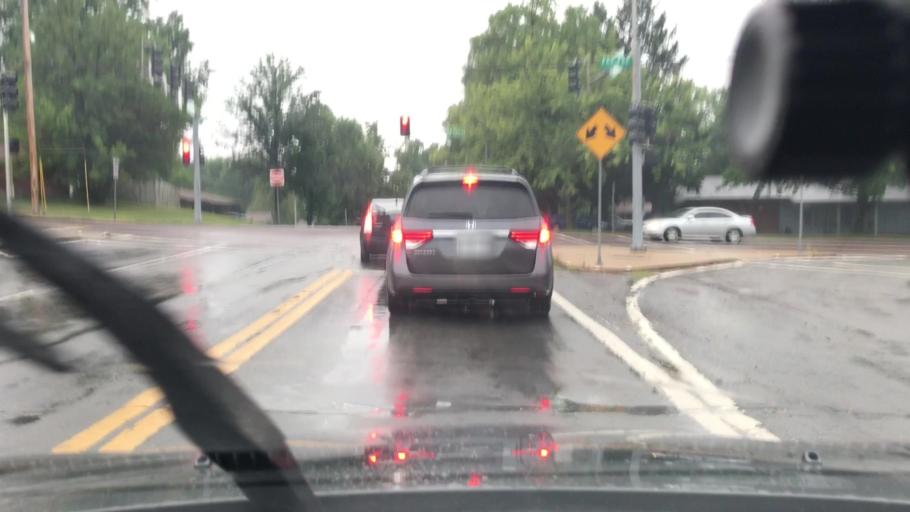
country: US
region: Missouri
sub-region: Saint Louis County
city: Maryland Heights
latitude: 38.6931
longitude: -90.4647
